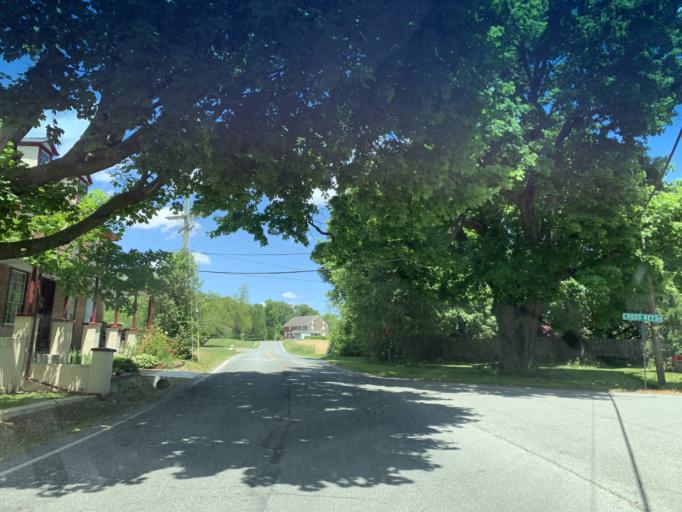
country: US
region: Maryland
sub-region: Cecil County
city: Rising Sun
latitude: 39.6990
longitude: -75.9842
